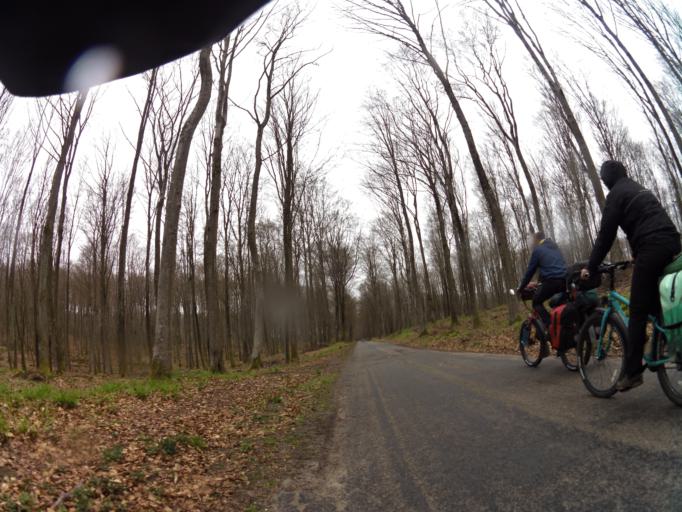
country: PL
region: West Pomeranian Voivodeship
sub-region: Powiat koszalinski
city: Bobolice
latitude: 53.9524
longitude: 16.6686
